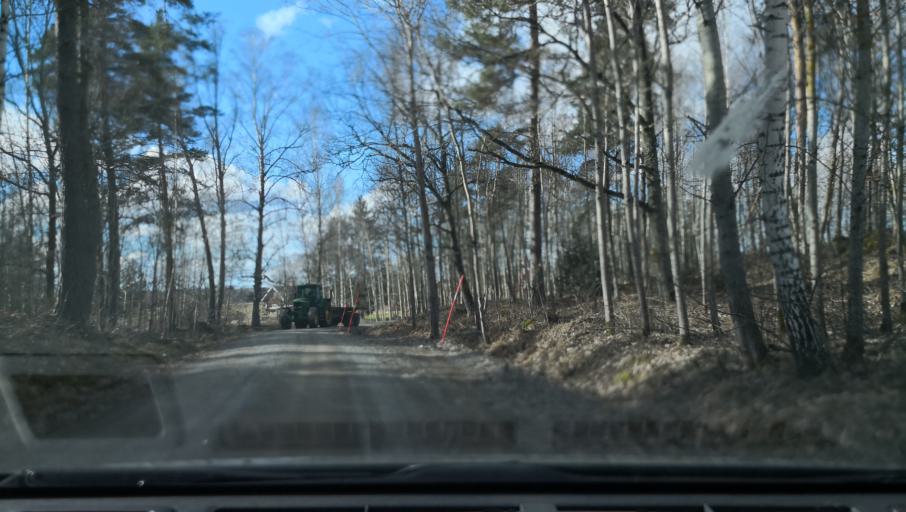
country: SE
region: OErebro
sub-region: Lindesbergs Kommun
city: Fellingsbro
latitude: 59.4227
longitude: 15.6930
